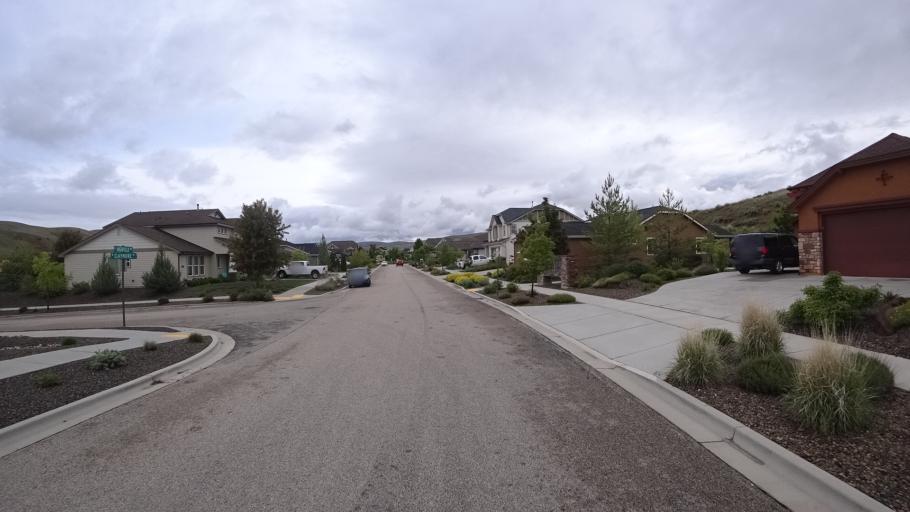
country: US
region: Idaho
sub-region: Ada County
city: Eagle
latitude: 43.7690
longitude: -116.2639
